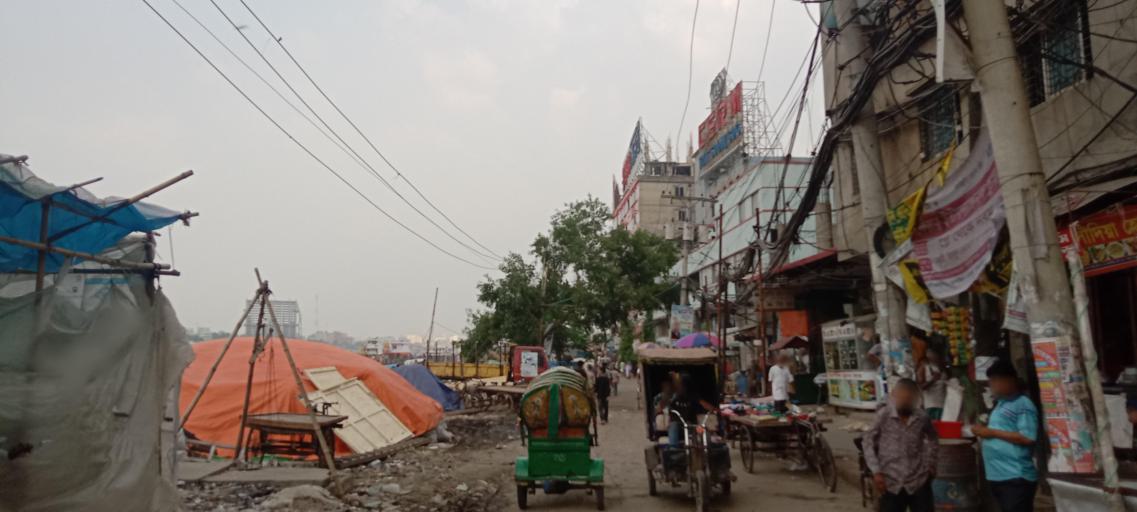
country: BD
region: Dhaka
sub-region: Dhaka
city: Dhaka
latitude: 23.7030
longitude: 90.4082
